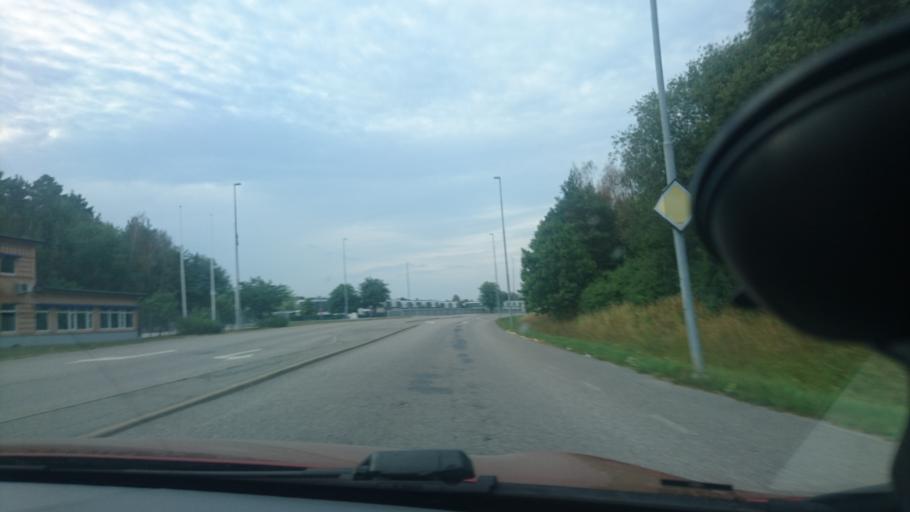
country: SE
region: Stockholm
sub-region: Upplands Vasby Kommun
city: Upplands Vaesby
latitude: 59.5040
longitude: 17.9151
